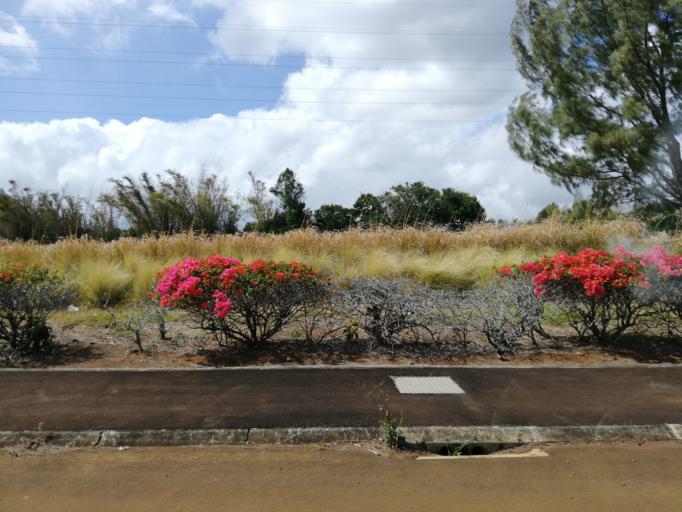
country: MU
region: Moka
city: Moka
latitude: -20.2247
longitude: 57.4807
